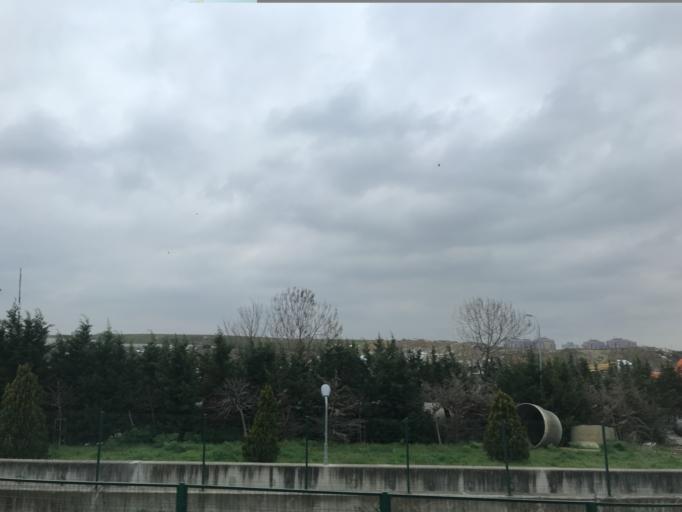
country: TR
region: Istanbul
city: Bahcelievler
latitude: 40.9758
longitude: 28.8433
